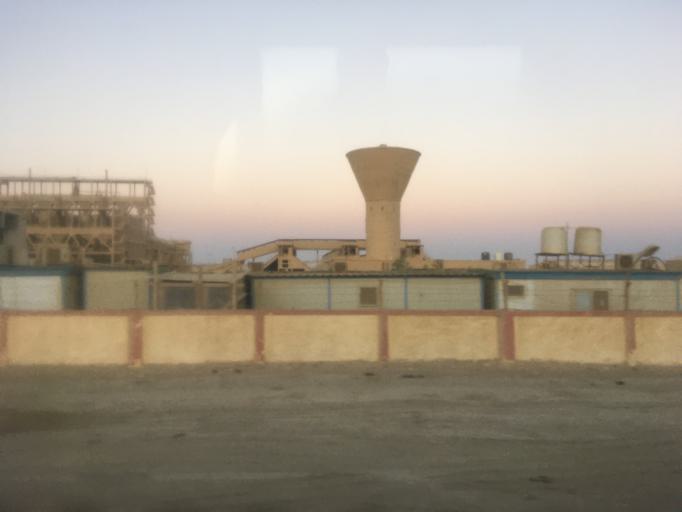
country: EG
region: Red Sea
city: Al Qusayr
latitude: 26.2563
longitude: 34.1995
